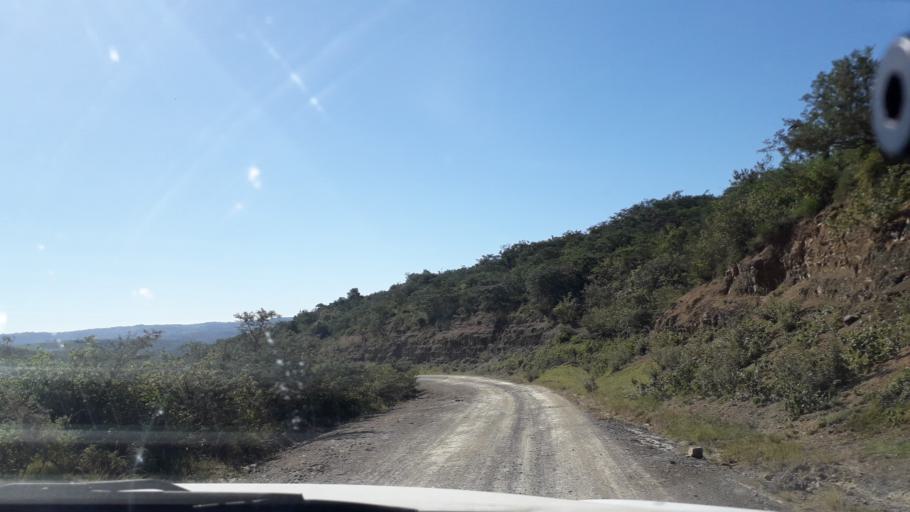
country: ZA
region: Eastern Cape
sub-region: Amathole District Municipality
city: Komga
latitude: -32.7809
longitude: 27.9576
